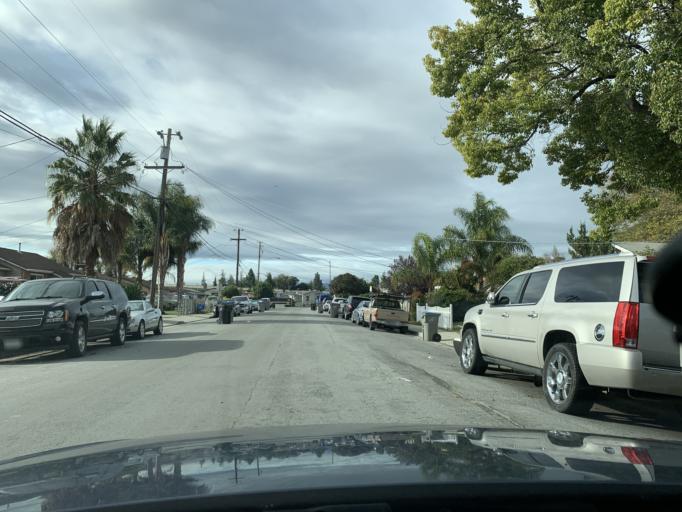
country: US
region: California
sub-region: Santa Clara County
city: Alum Rock
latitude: 37.3437
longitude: -121.8517
